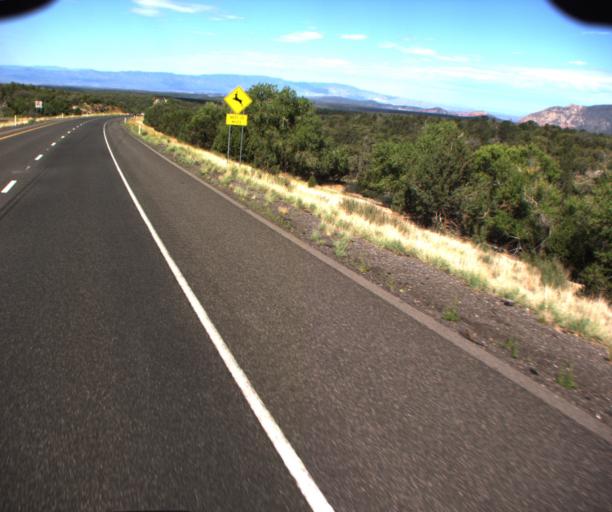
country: US
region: Arizona
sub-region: Yavapai County
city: Village of Oak Creek (Big Park)
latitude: 34.7829
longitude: -111.6131
